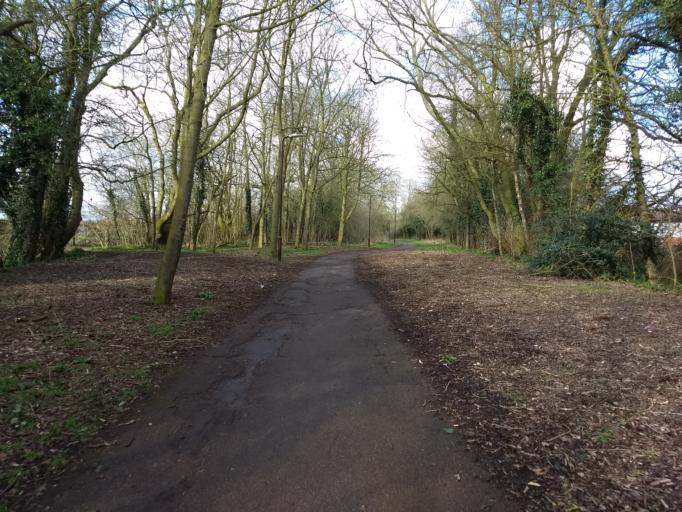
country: GB
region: England
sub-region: Milton Keynes
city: Milton Keynes
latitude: 52.0232
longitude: -0.7501
